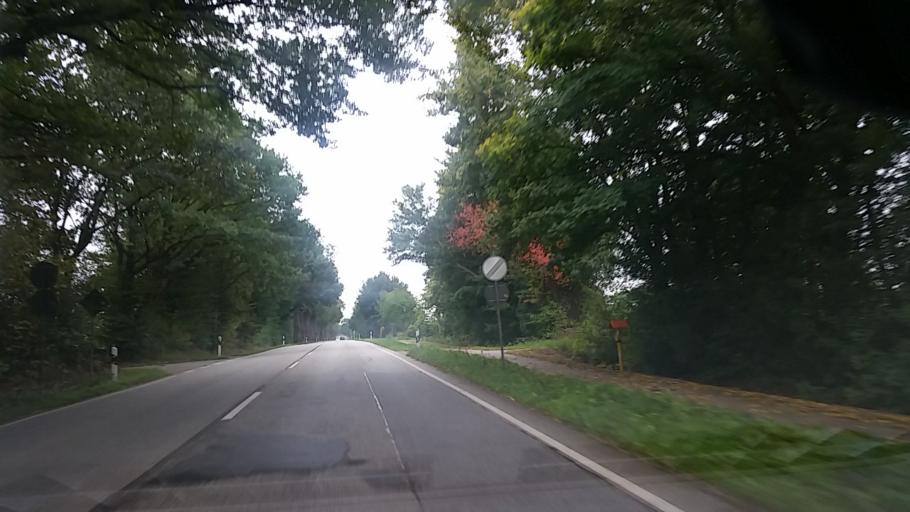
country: DE
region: Schleswig-Holstein
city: Mozen
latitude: 53.9052
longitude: 10.2623
